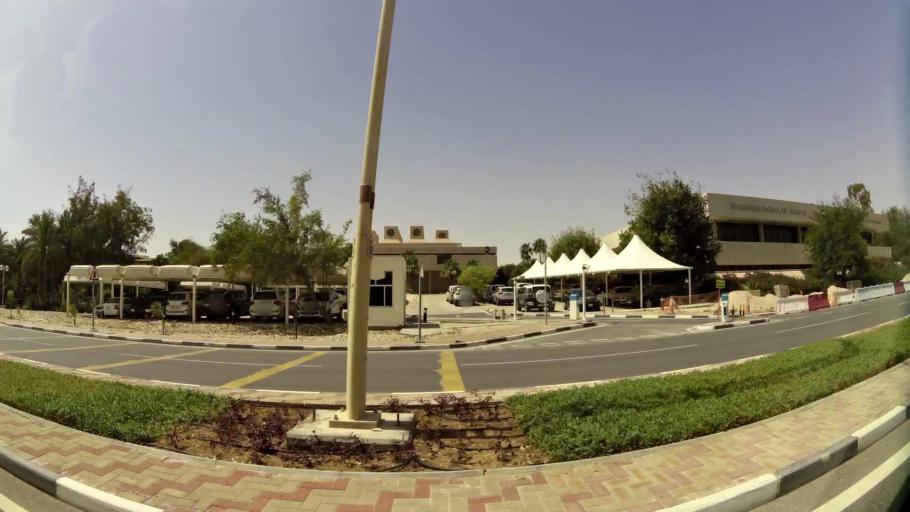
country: QA
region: Baladiyat Umm Salal
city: Umm Salal Muhammad
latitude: 25.3745
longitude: 51.4936
